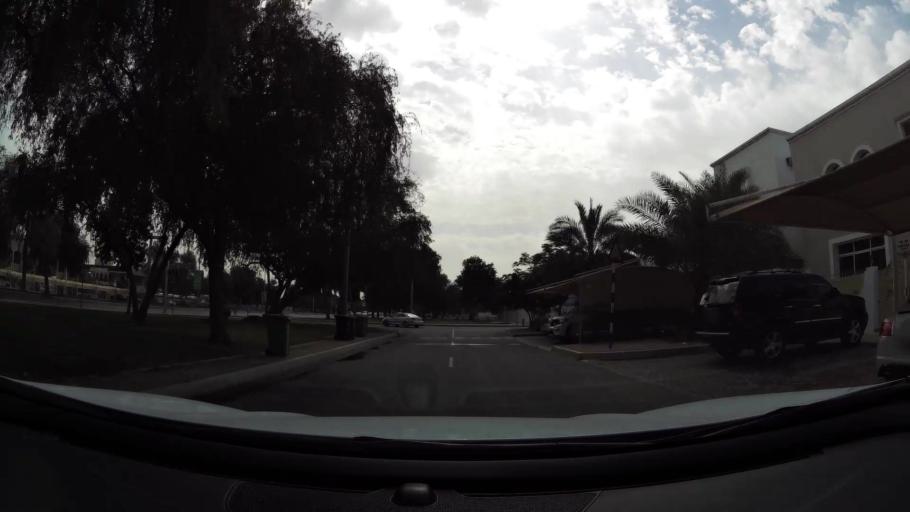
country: AE
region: Abu Dhabi
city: Abu Dhabi
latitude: 24.4407
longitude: 54.3702
